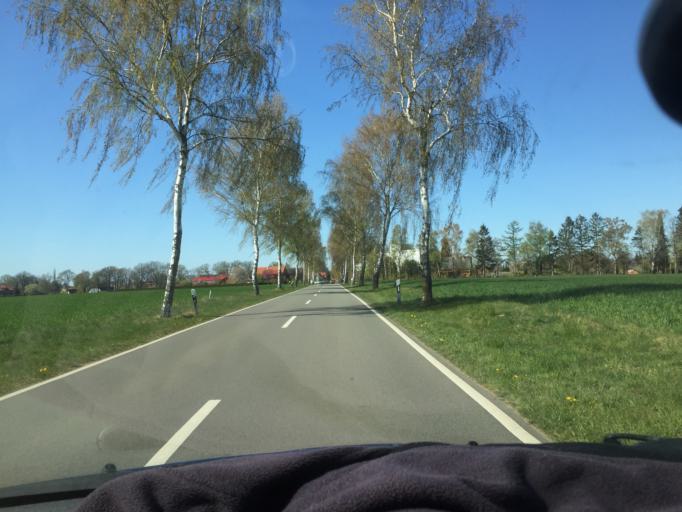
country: DE
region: Lower Saxony
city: Tosterglope
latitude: 53.2386
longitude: 10.7907
